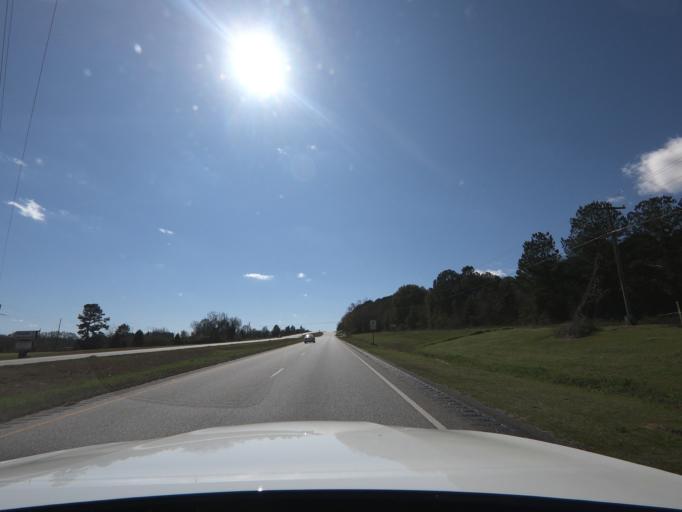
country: US
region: Alabama
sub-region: Barbour County
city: Eufaula
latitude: 31.7861
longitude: -85.1734
